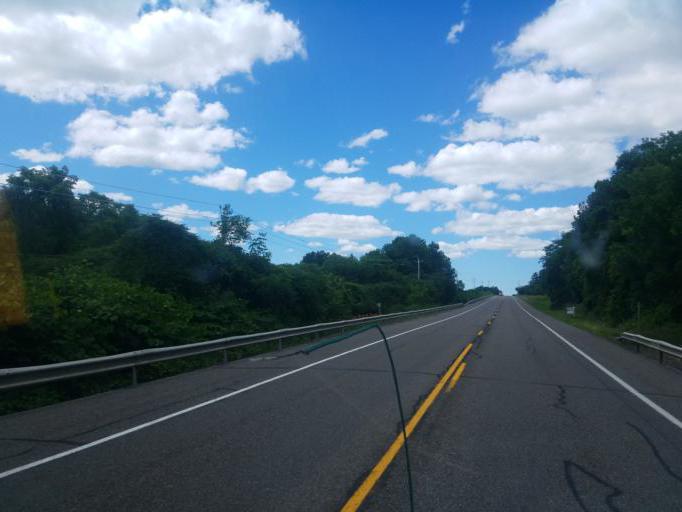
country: US
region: New York
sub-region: Wayne County
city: Lyons
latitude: 43.0011
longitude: -76.9804
